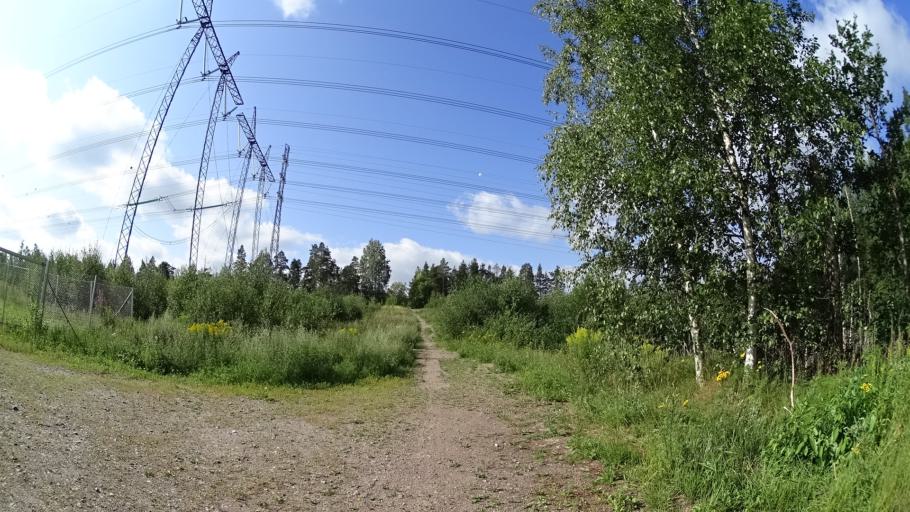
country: FI
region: Uusimaa
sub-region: Helsinki
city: Teekkarikylae
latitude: 60.2933
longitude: 24.9048
